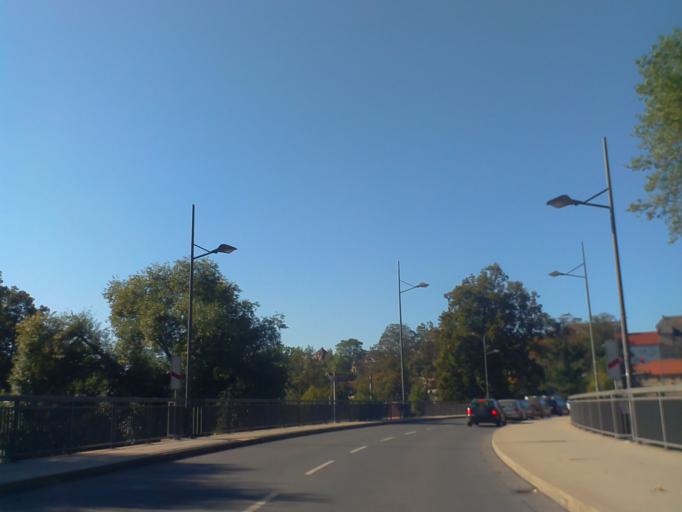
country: DE
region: Thuringia
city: Kahla
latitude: 50.8005
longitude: 11.5914
